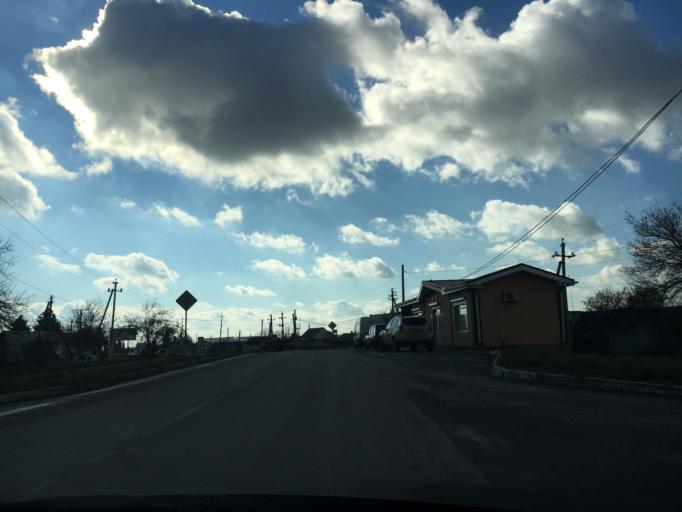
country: RU
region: Rostov
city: Matveyev Kurgan
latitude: 47.5595
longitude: 38.8719
